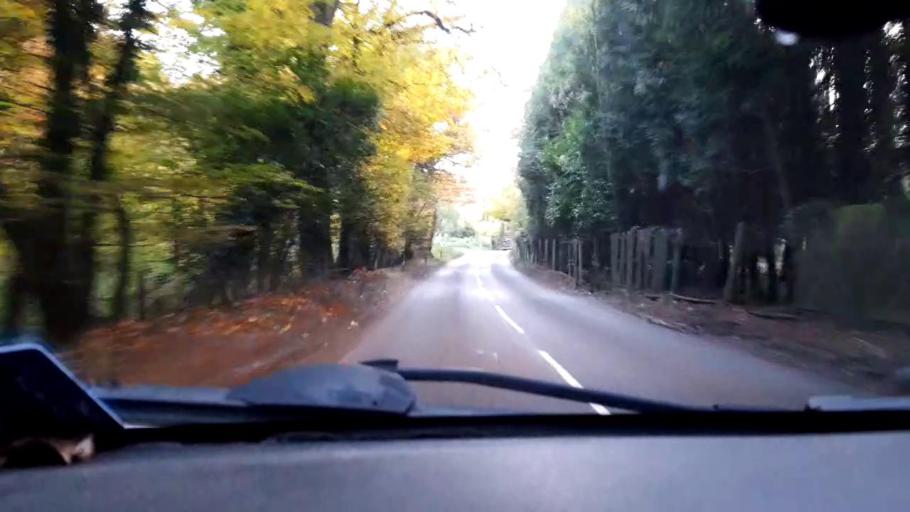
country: GB
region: England
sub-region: Norfolk
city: Mattishall
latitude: 52.7192
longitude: 1.1137
